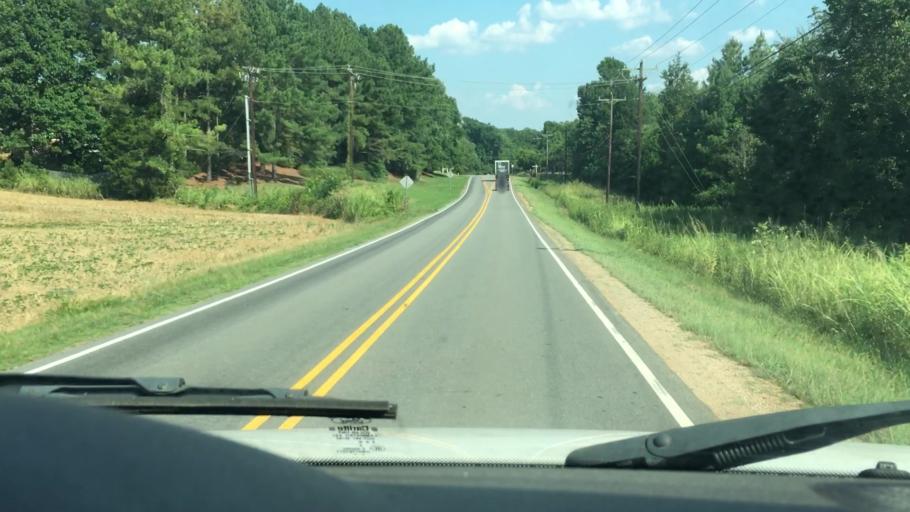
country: US
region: North Carolina
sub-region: Gaston County
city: Davidson
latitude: 35.4656
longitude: -80.8131
